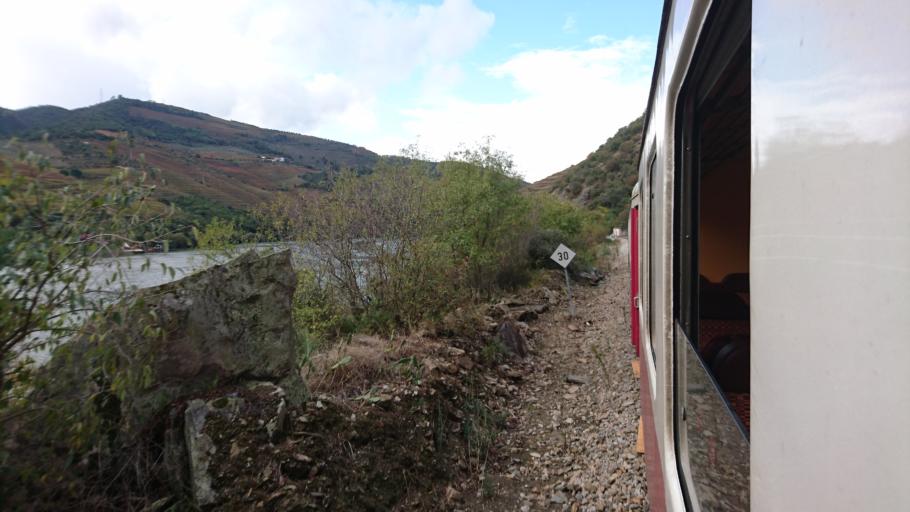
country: PT
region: Viseu
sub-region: Tabuaco
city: Tabuaco
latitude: 41.1604
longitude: -7.5813
